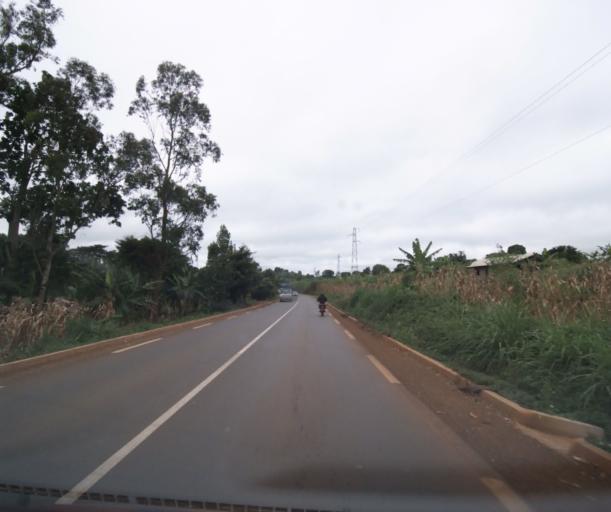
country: CM
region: West
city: Bansoa
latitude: 5.5414
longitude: 10.3275
